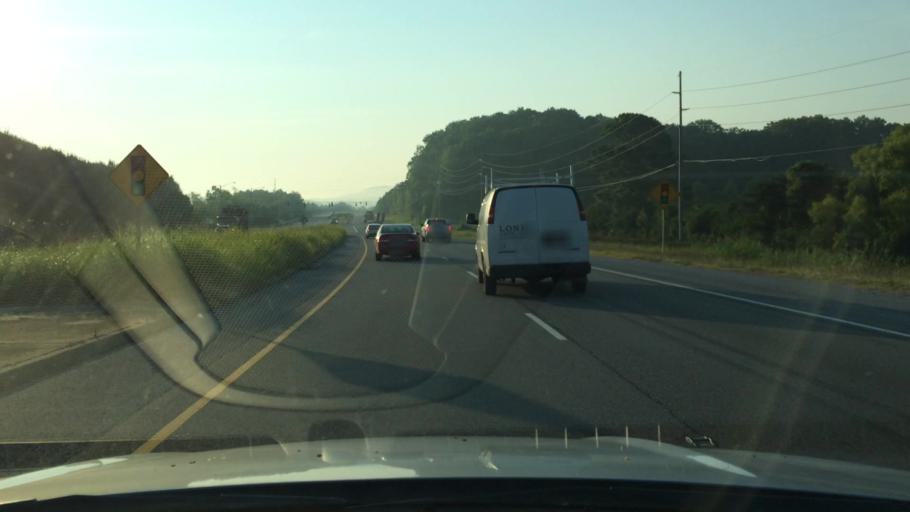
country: US
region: Tennessee
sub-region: Giles County
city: Pulaski
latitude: 35.1705
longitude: -87.0540
